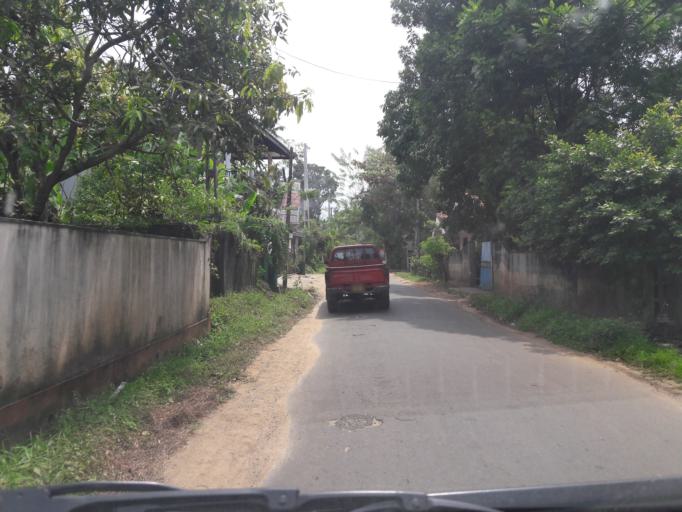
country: LK
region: Southern
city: Hikkaduwa
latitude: 6.0952
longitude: 80.1476
